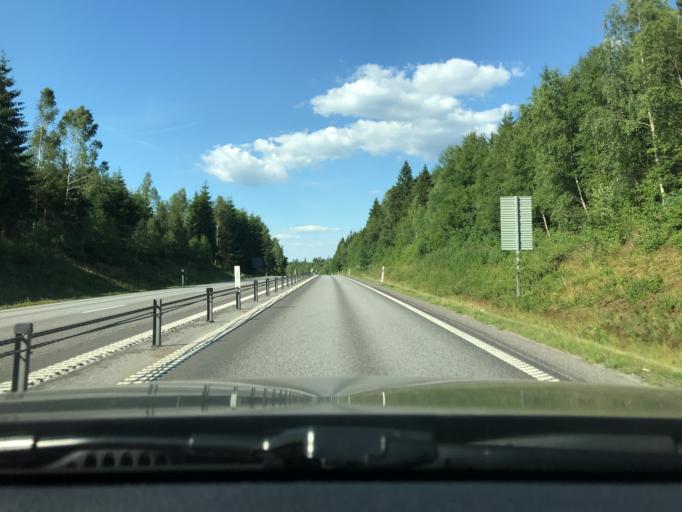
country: SE
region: Kronoberg
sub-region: Almhults Kommun
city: AElmhult
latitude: 56.4626
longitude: 14.0989
